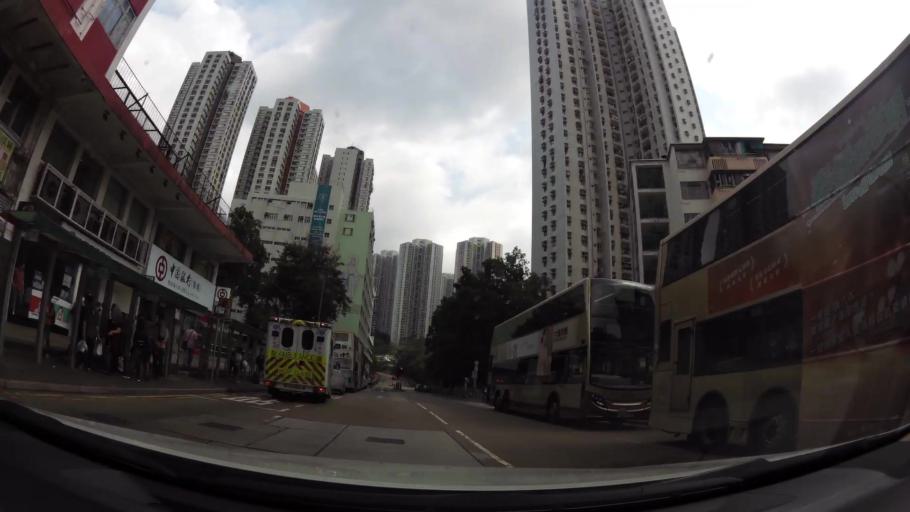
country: HK
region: Kowloon City
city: Kowloon
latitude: 22.3171
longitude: 114.2266
